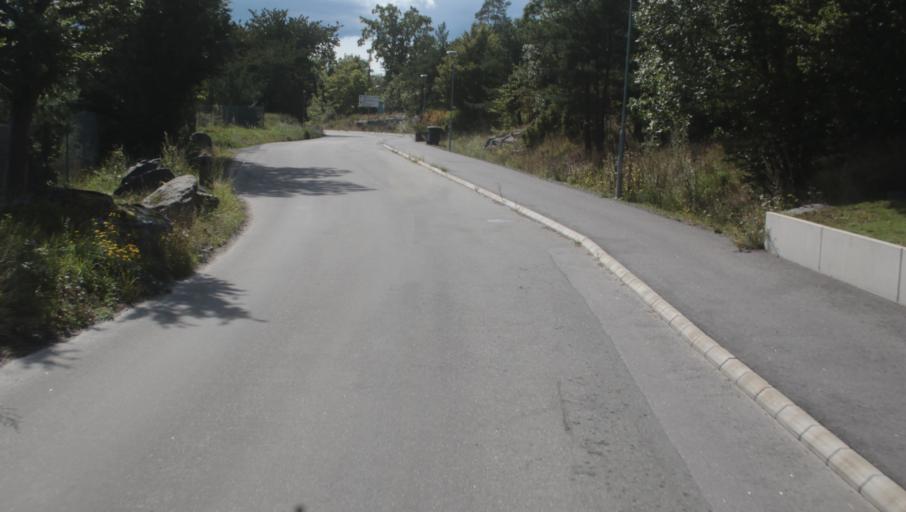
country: SE
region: Blekinge
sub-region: Karlshamns Kommun
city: Karlshamn
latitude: 56.1470
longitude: 14.8476
